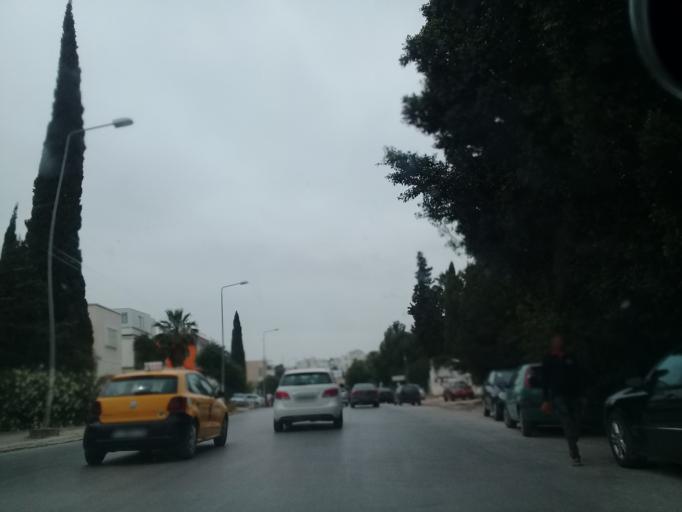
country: TN
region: Tunis
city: Tunis
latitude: 36.8416
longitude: 10.1628
